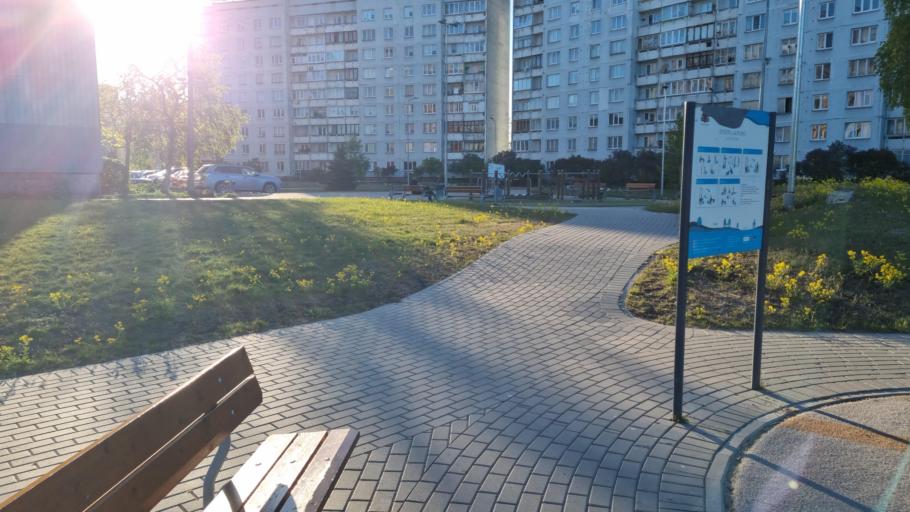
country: LV
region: Riga
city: Bolderaja
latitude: 57.0327
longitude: 24.0561
